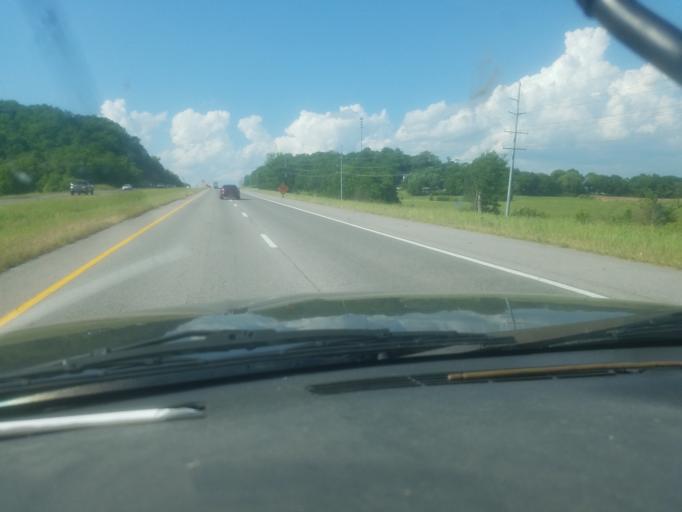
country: US
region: Tennessee
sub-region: Maury County
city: Mount Pleasant
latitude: 35.5311
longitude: -87.2218
